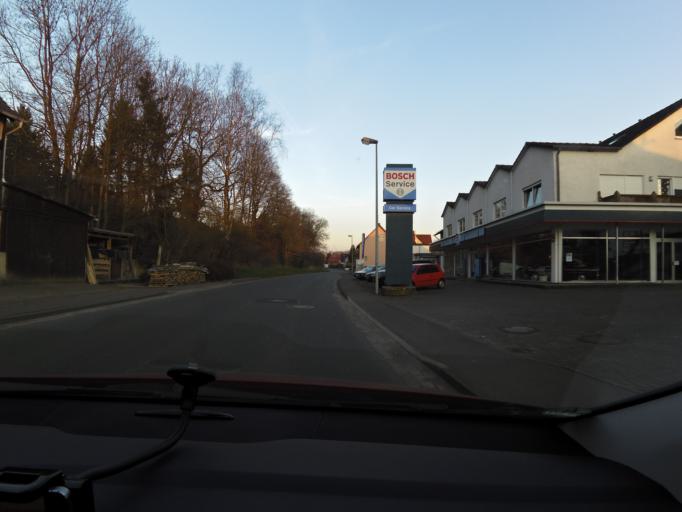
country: DE
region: Hesse
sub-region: Regierungsbezirk Kassel
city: Nieste
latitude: 51.3289
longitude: 9.6249
